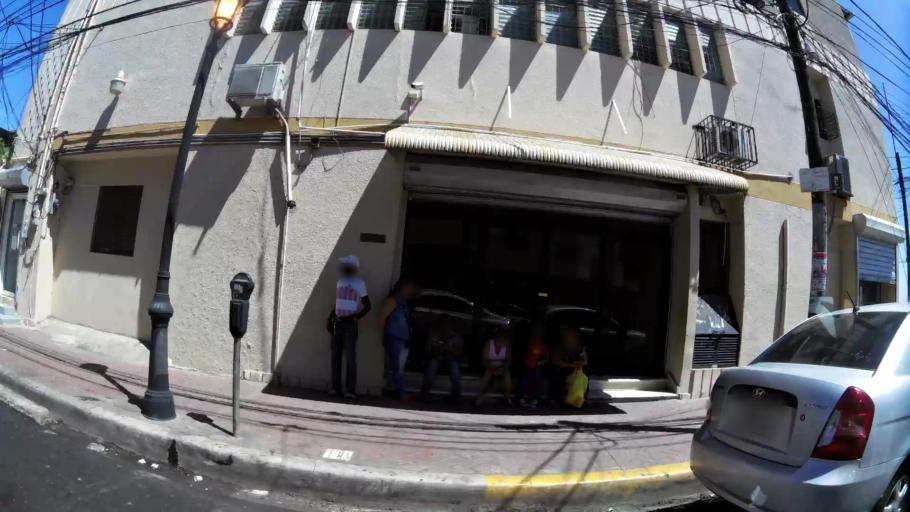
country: DO
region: Santiago
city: Santiago de los Caballeros
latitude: 19.4496
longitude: -70.7064
